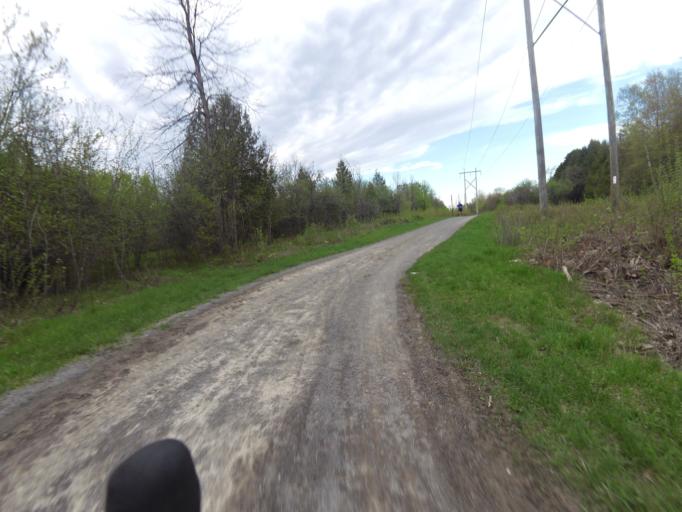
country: CA
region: Ontario
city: Bells Corners
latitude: 45.2819
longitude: -75.8031
